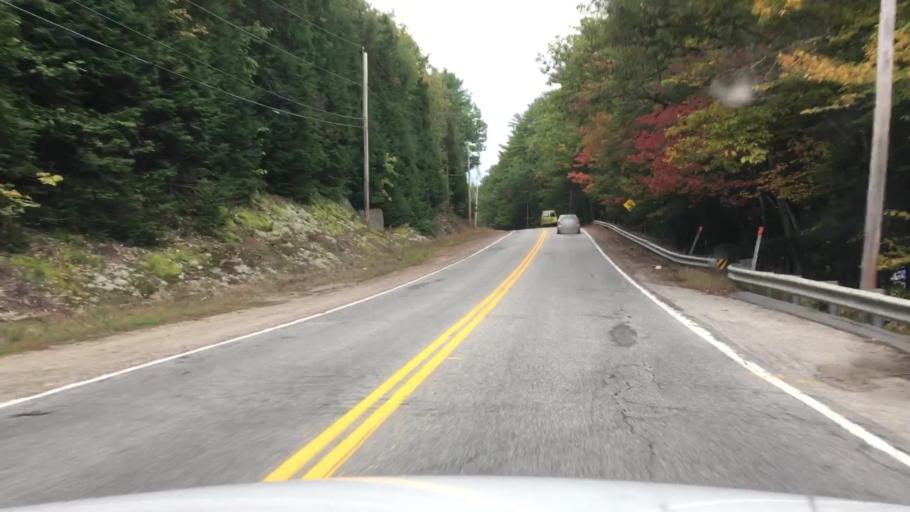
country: US
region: Maine
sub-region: Oxford County
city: Norway
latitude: 44.2205
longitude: -70.6100
